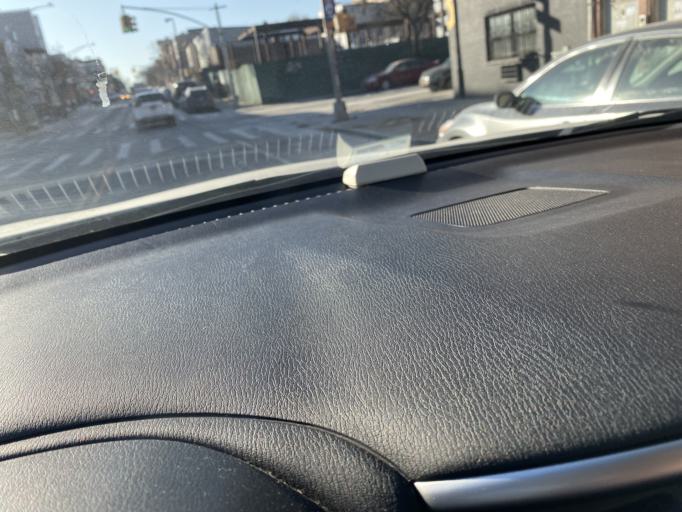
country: US
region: New York
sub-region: Kings County
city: Brooklyn
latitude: 40.6761
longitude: -73.9305
